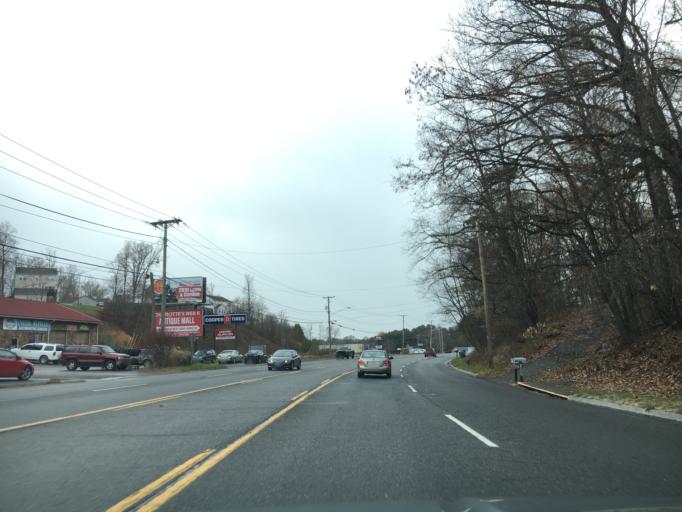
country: US
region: Virginia
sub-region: Montgomery County
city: Christiansburg
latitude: 37.1328
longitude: -80.3820
